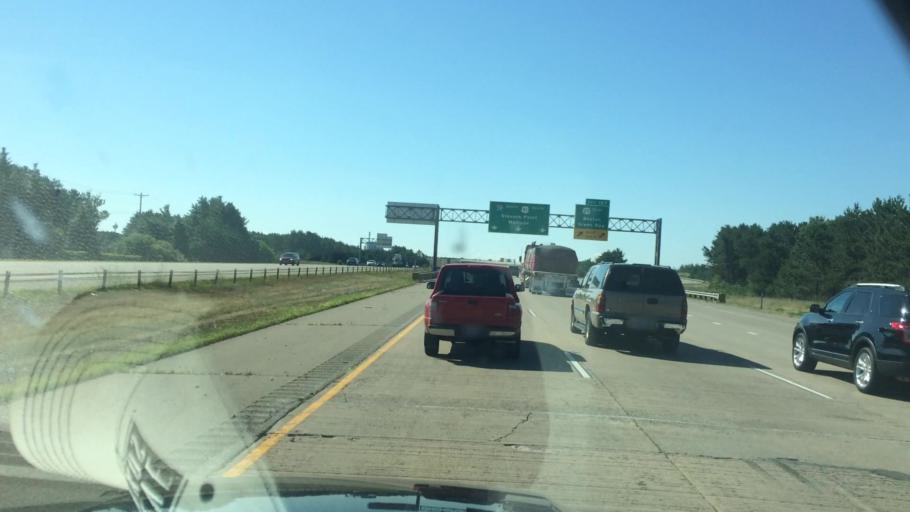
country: US
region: Wisconsin
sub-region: Marathon County
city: Rothschild
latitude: 44.9040
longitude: -89.6455
